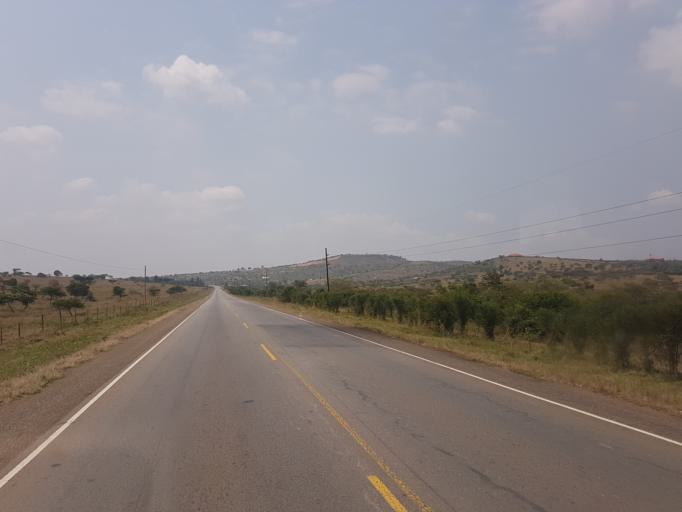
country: UG
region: Western Region
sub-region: Mbarara District
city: Mbarara
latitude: -0.5076
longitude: 30.8421
